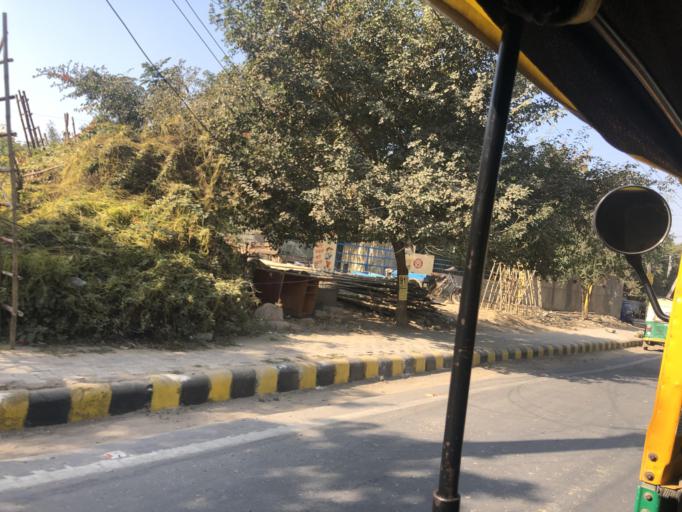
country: IN
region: Haryana
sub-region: Gurgaon
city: Gurgaon
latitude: 28.4468
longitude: 77.0753
